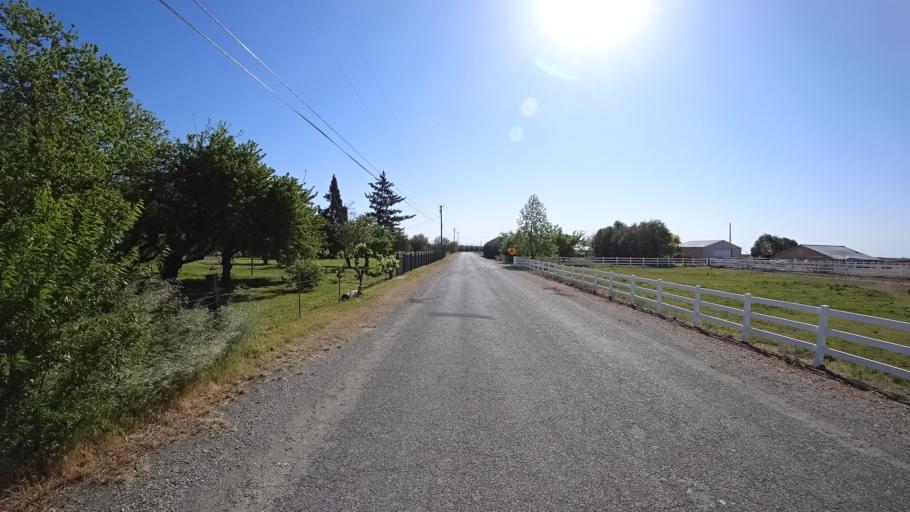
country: US
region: California
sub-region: Glenn County
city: Orland
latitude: 39.7289
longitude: -122.1531
